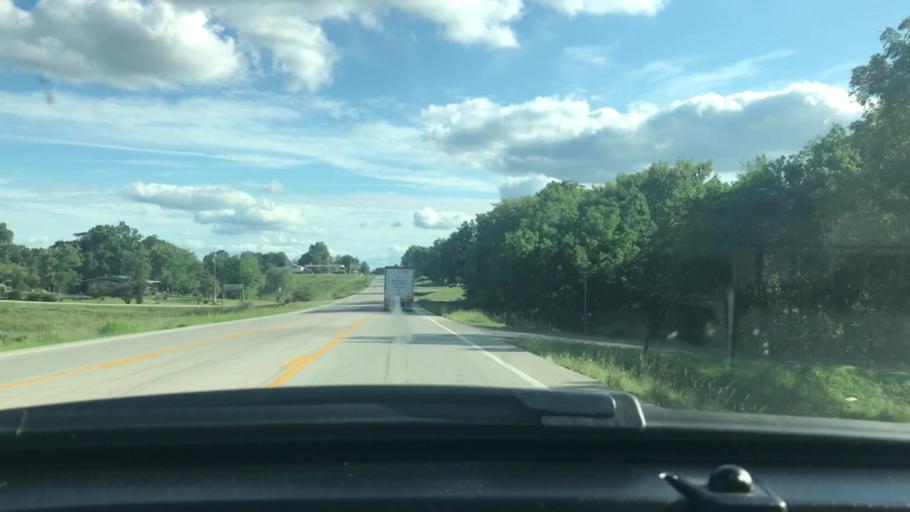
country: US
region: Missouri
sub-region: Oregon County
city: Thayer
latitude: 36.5994
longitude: -91.6440
